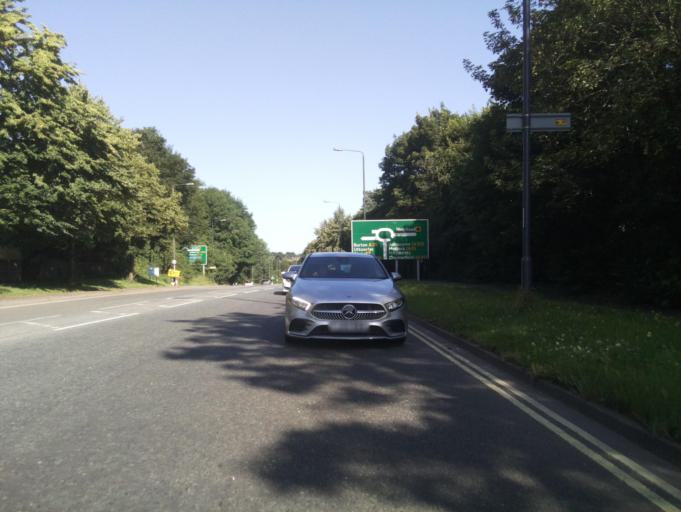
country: GB
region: England
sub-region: Derby
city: Derby
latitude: 52.9196
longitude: -1.5095
